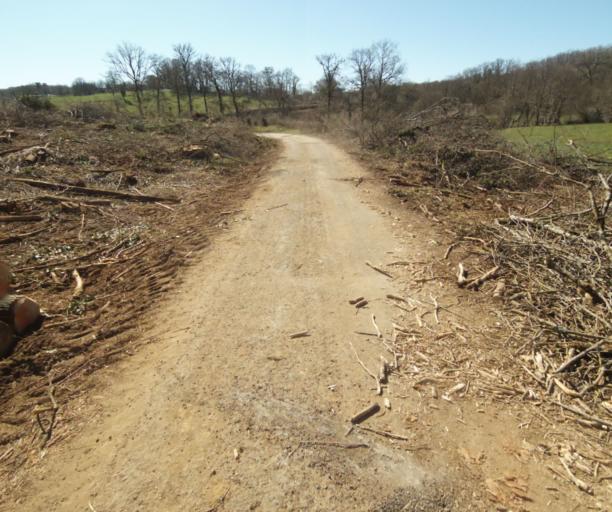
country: FR
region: Limousin
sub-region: Departement de la Correze
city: Chamboulive
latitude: 45.4095
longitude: 1.7430
